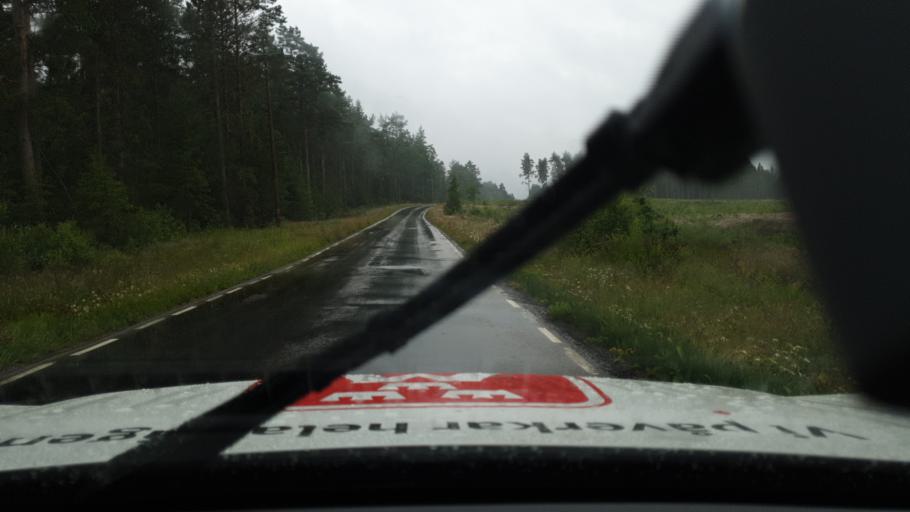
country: SE
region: Vaestra Goetaland
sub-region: Falkopings Kommun
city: Floby
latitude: 58.1728
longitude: 13.3449
